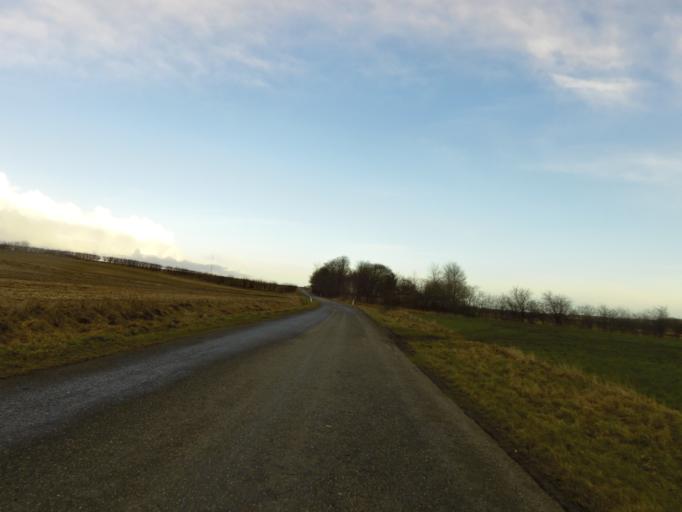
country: DK
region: South Denmark
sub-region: Haderslev Kommune
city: Gram
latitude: 55.2627
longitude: 9.1030
